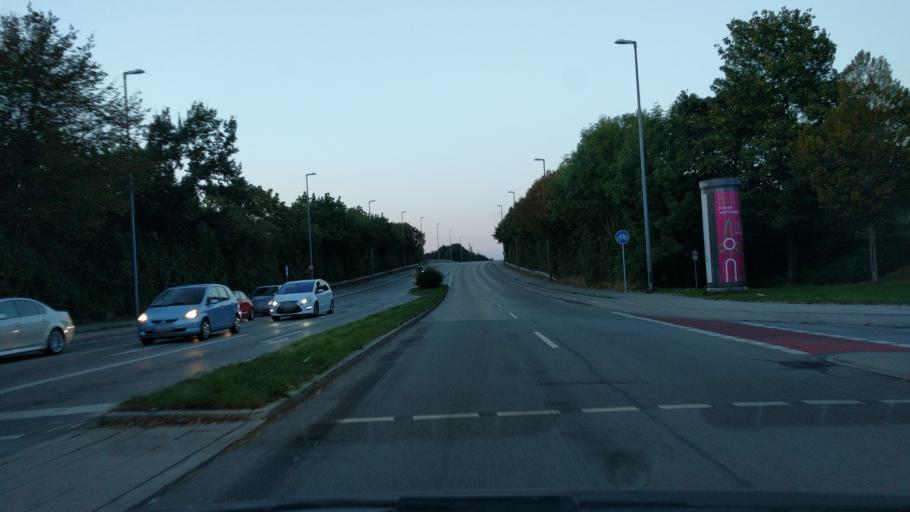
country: DE
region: Bavaria
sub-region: Upper Bavaria
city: Bogenhausen
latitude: 48.1260
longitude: 11.6549
